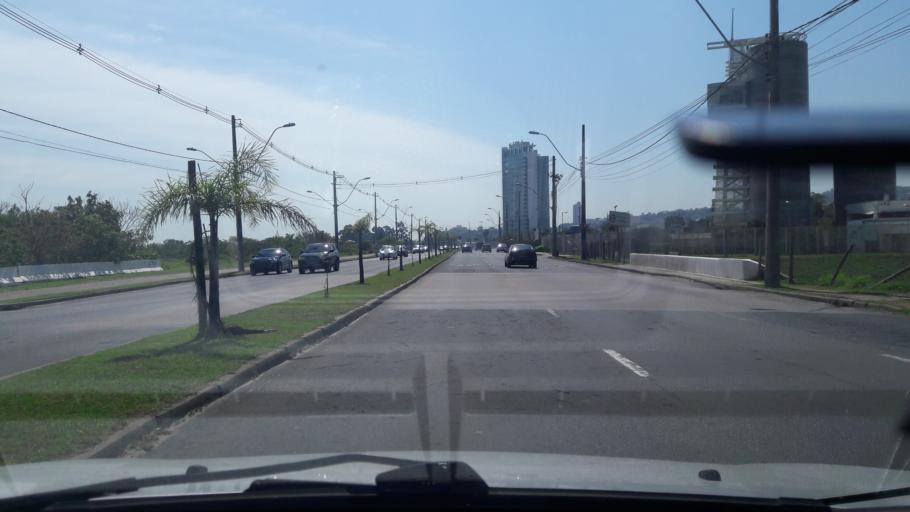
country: BR
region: Rio Grande do Sul
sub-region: Porto Alegre
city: Porto Alegre
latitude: -30.0920
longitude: -51.2491
